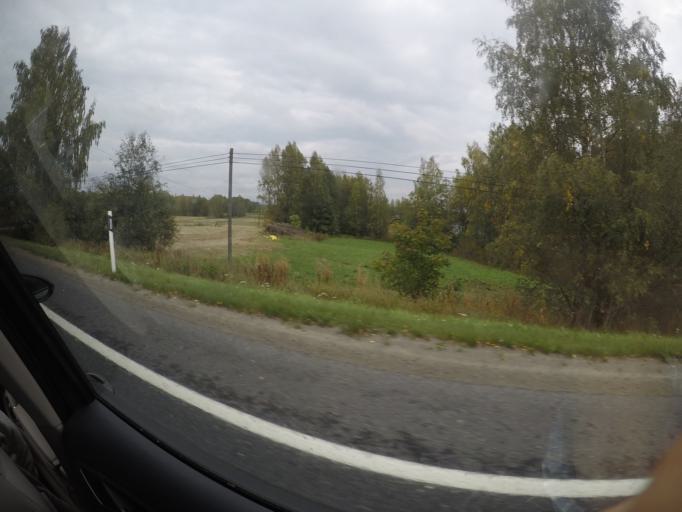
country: FI
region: Haeme
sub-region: Haemeenlinna
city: Parola
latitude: 61.0662
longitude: 24.3925
